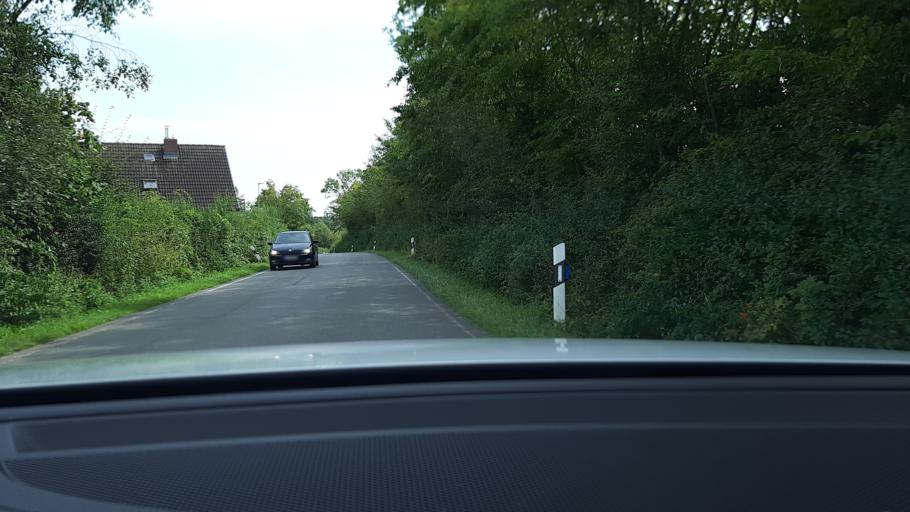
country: DE
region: Schleswig-Holstein
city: Reinfeld
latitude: 53.8409
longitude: 10.4738
